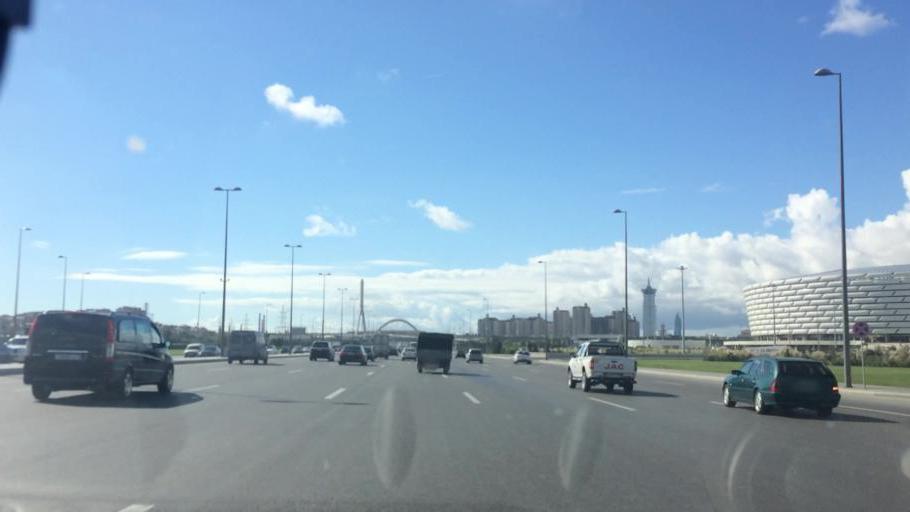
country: AZ
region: Baki
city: Sabuncu
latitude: 40.4325
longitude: 49.9277
